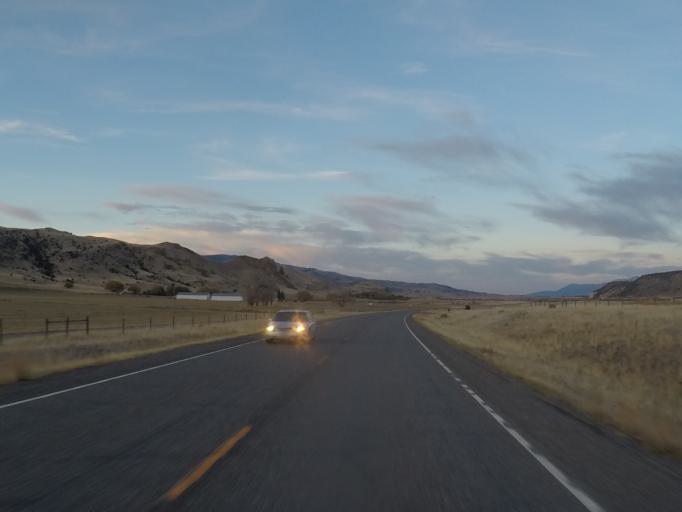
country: US
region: Montana
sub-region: Gallatin County
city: Bozeman
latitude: 45.2729
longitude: -110.8591
